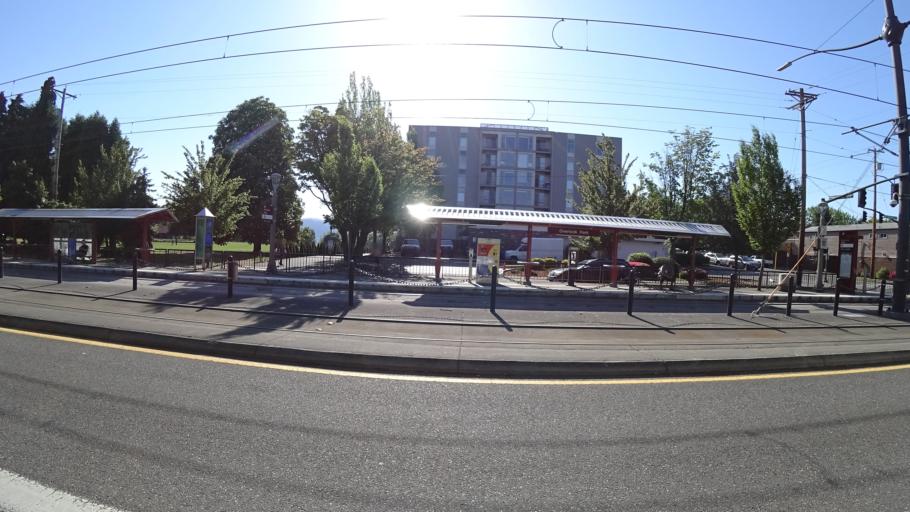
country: US
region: Oregon
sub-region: Multnomah County
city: Portland
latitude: 45.5492
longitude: -122.6809
